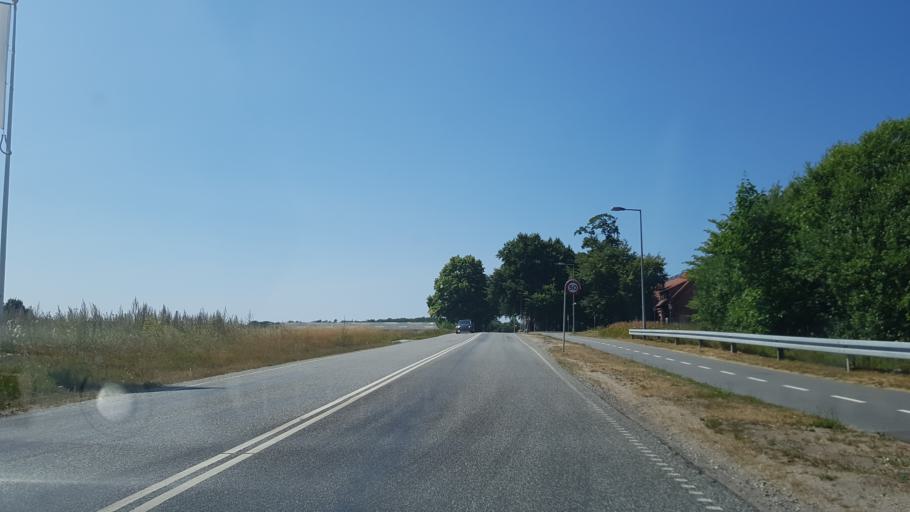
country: DK
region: Capital Region
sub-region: Allerod Kommune
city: Blovstrod
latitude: 55.8651
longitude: 12.3774
